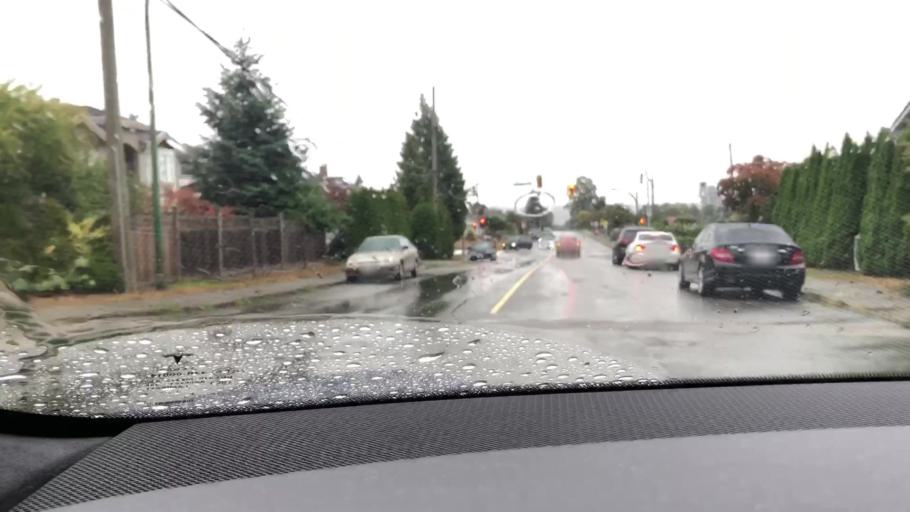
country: CA
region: British Columbia
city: New Westminster
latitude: 49.2280
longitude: -122.9130
